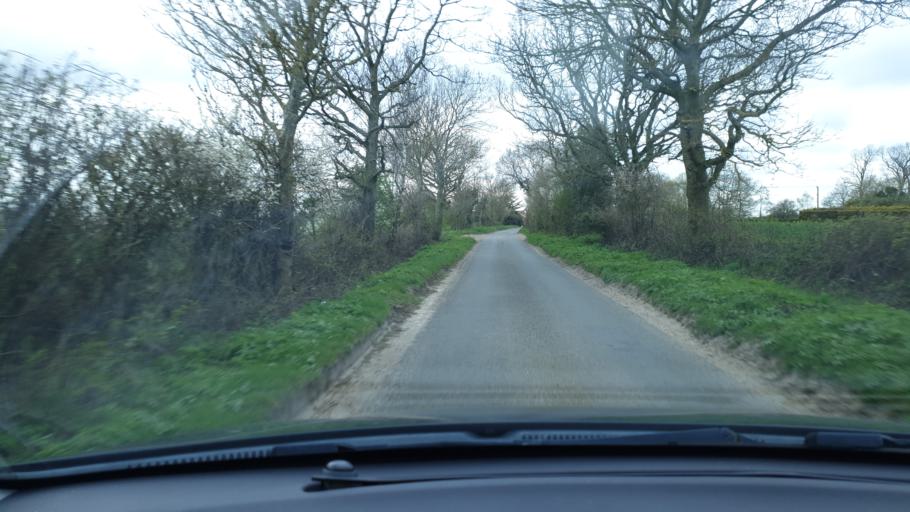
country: GB
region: England
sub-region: Essex
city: Mistley
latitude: 51.9049
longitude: 1.1204
